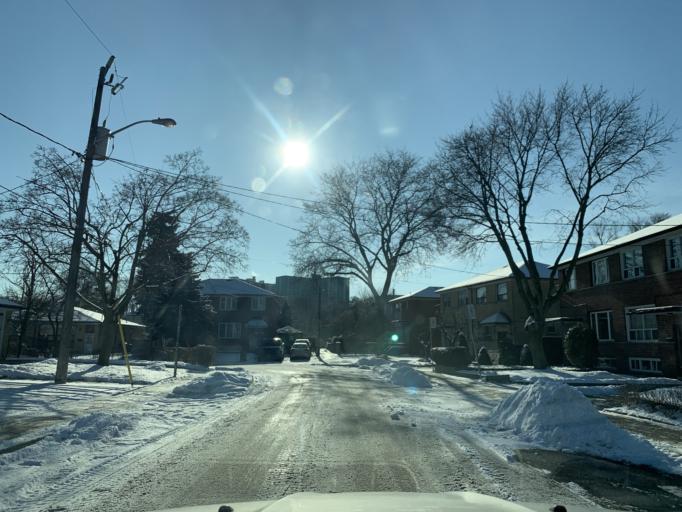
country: CA
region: Ontario
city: Etobicoke
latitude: 43.6772
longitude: -79.4935
